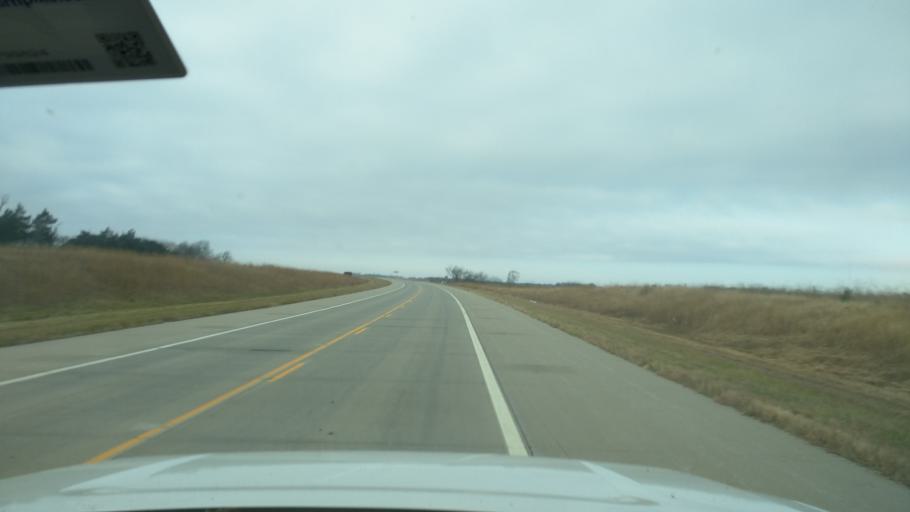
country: US
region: Kansas
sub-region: Elk County
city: Howard
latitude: 37.6373
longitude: -96.2393
